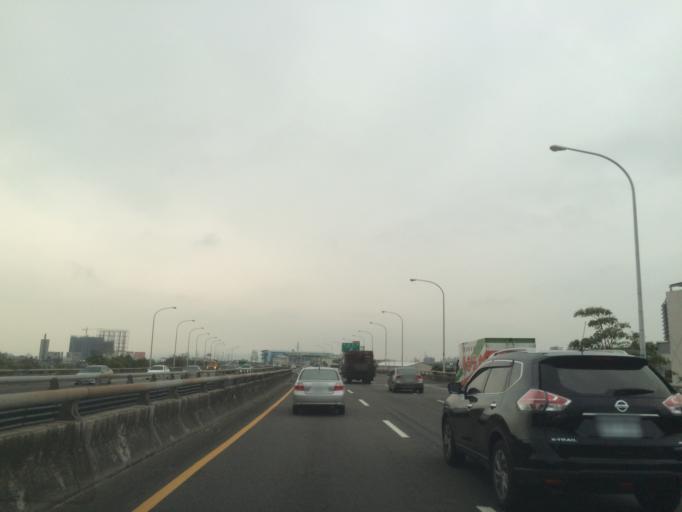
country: TW
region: Taiwan
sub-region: Taichung City
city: Taichung
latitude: 24.1550
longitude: 120.6246
